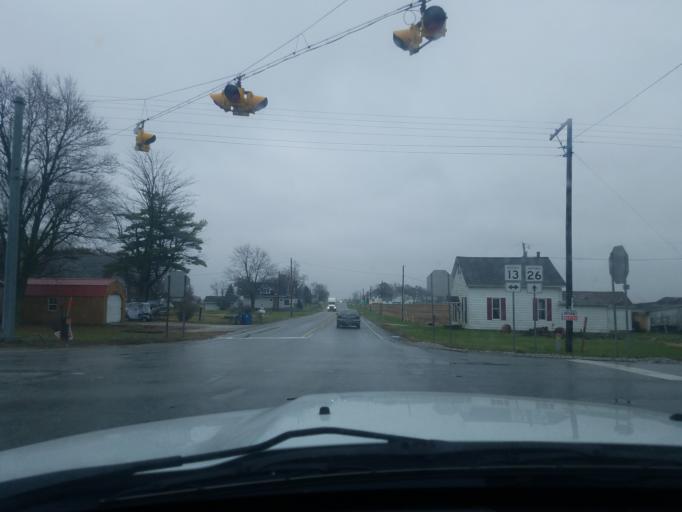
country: US
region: Indiana
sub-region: Madison County
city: Elwood
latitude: 40.4215
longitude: -85.8247
